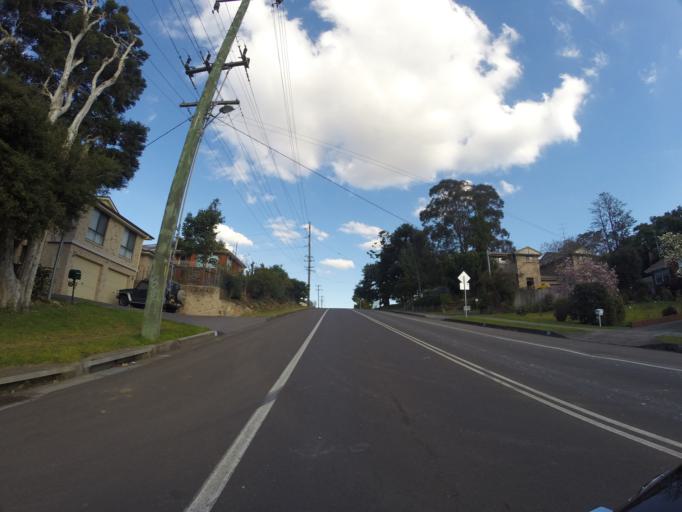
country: AU
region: New South Wales
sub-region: Wollongong
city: Keiraville
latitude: -34.4193
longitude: 150.8694
